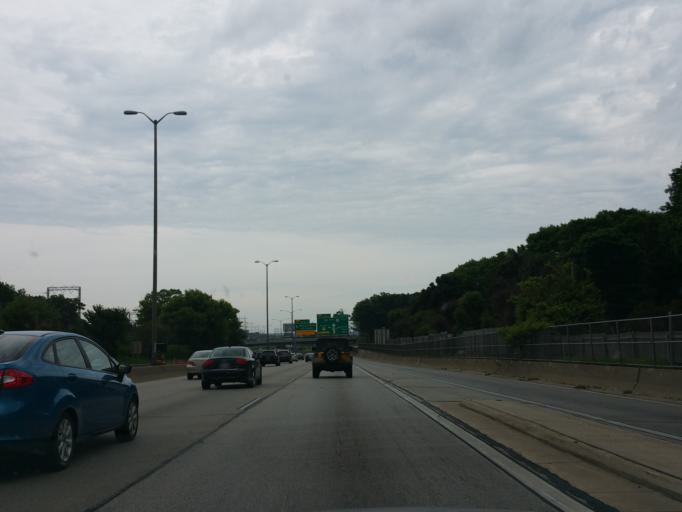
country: US
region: Wisconsin
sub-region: Milwaukee County
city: West Milwaukee
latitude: 43.0304
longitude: -87.9850
